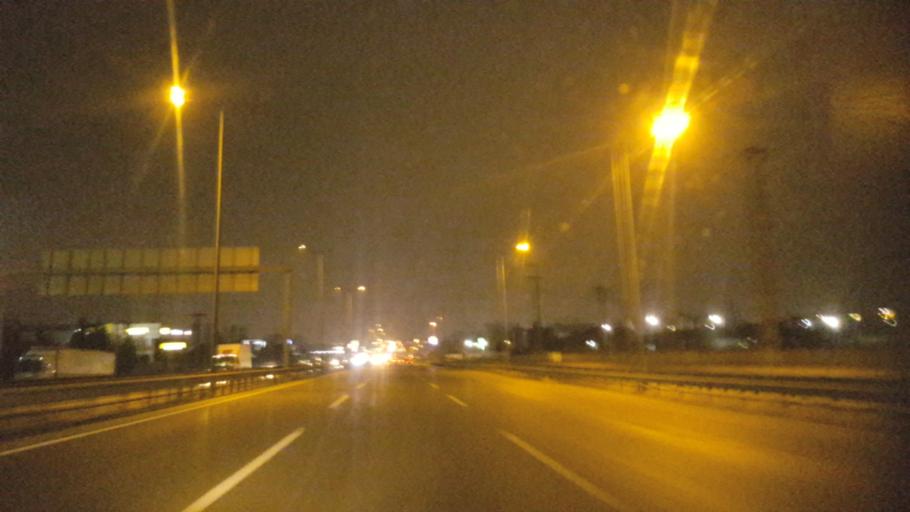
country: TR
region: Kocaeli
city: Darica
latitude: 40.8051
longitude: 29.3765
